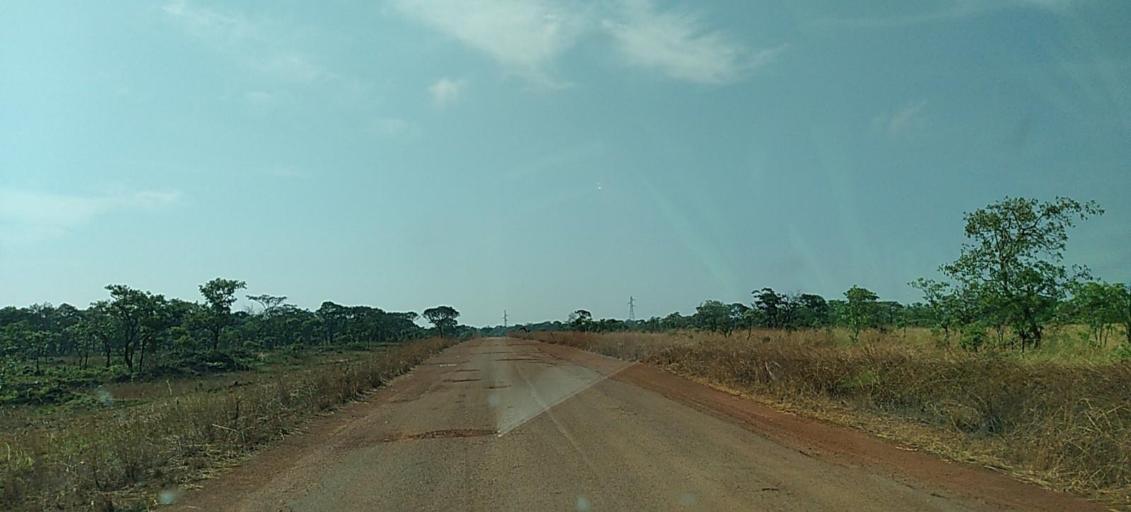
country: ZM
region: North-Western
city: Mwinilunga
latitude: -11.7809
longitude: 25.0231
